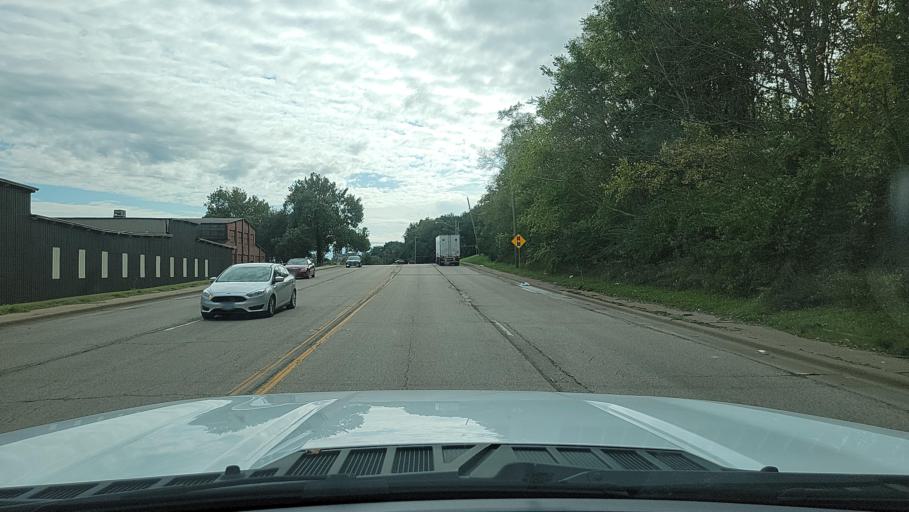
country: US
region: Illinois
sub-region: Peoria County
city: Bartonville
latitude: 40.6434
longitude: -89.6514
